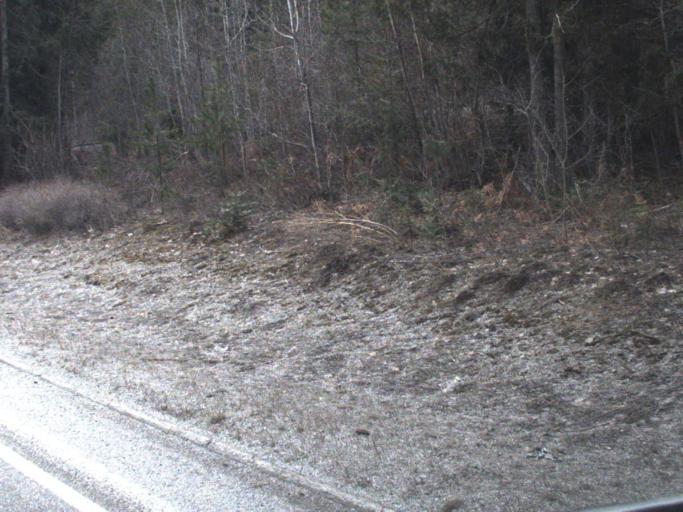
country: US
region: Washington
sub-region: Pend Oreille County
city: Newport
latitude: 48.5389
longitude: -117.3041
